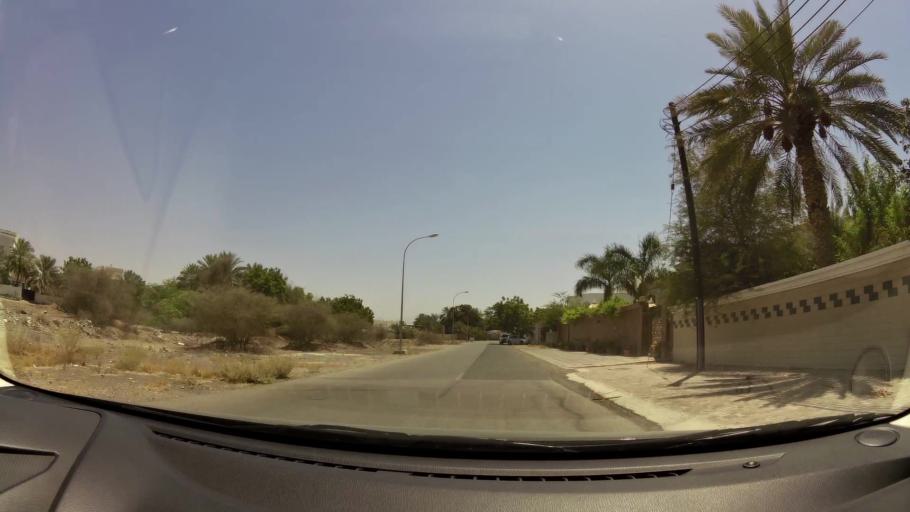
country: OM
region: Muhafazat Masqat
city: As Sib al Jadidah
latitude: 23.6191
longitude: 58.2298
